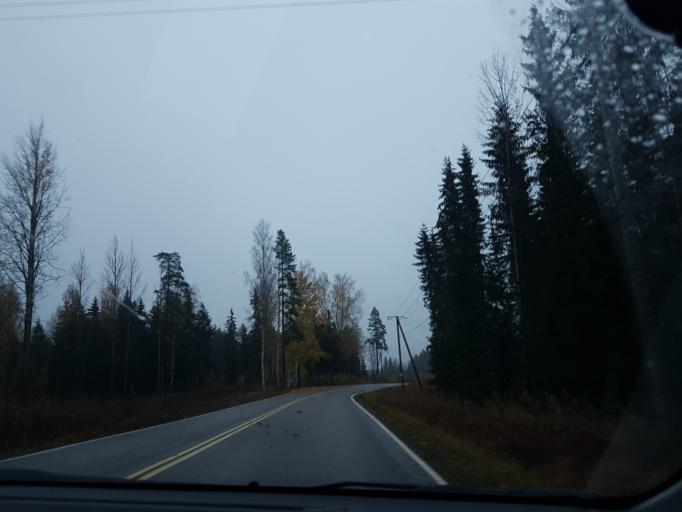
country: FI
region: Uusimaa
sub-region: Helsinki
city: Maentsaelae
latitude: 60.5935
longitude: 25.1922
